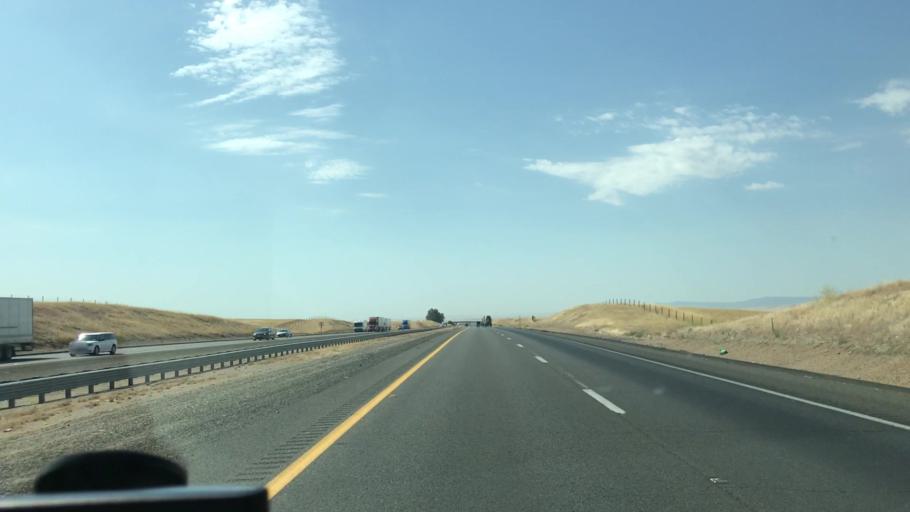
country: US
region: California
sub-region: Merced County
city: Gustine
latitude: 37.1720
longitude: -121.0599
